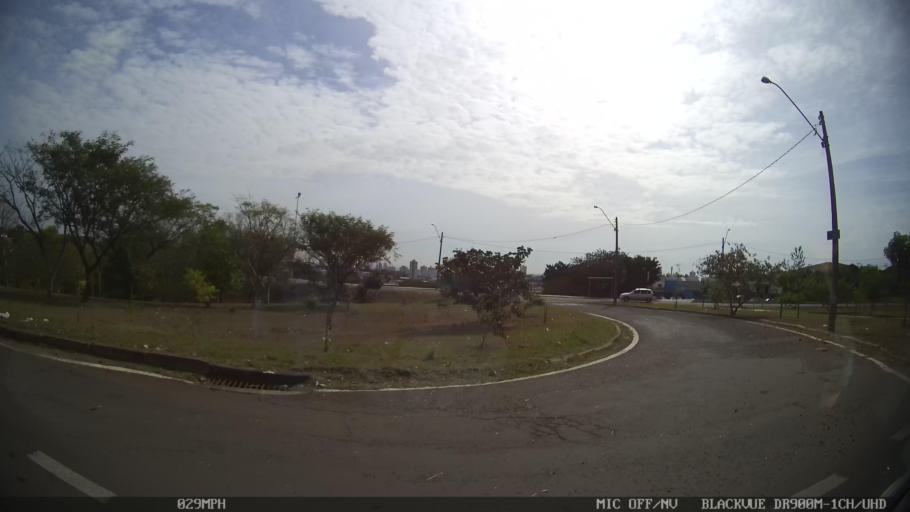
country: BR
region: Sao Paulo
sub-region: Piracicaba
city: Piracicaba
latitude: -22.7570
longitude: -47.6424
